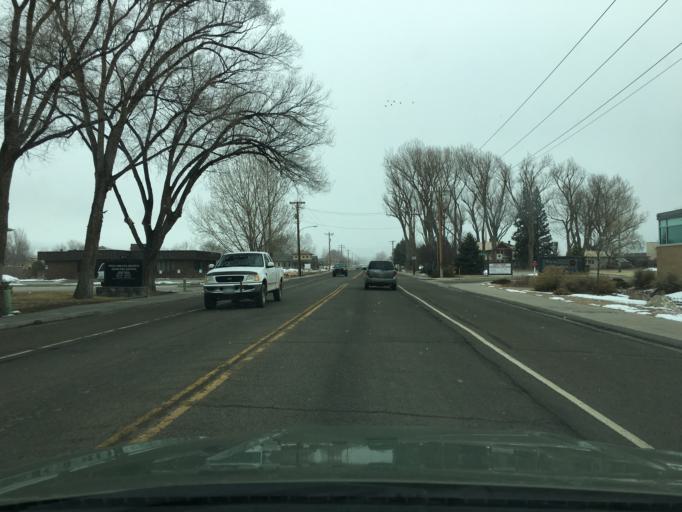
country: US
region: Colorado
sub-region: Montrose County
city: Montrose
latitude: 38.4672
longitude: -107.8632
